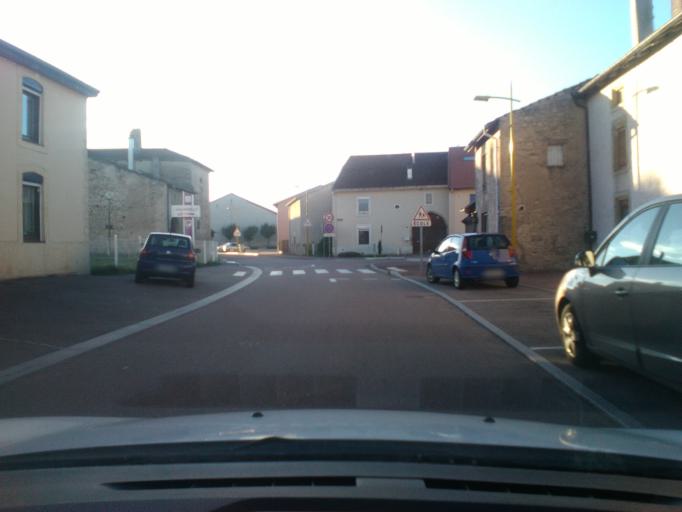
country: FR
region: Lorraine
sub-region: Departement des Vosges
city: Vincey
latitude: 48.3377
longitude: 6.3328
